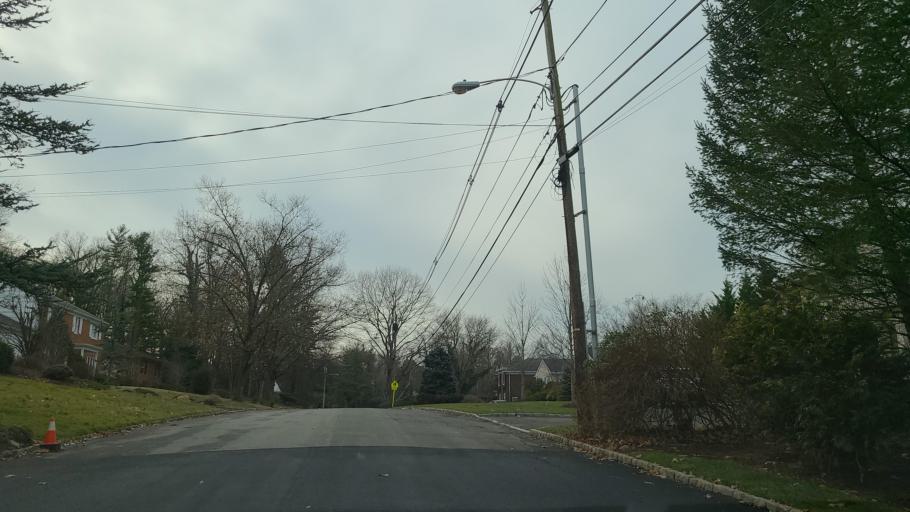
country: US
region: New Jersey
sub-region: Essex County
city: Short Hills
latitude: 40.7544
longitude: -74.3134
